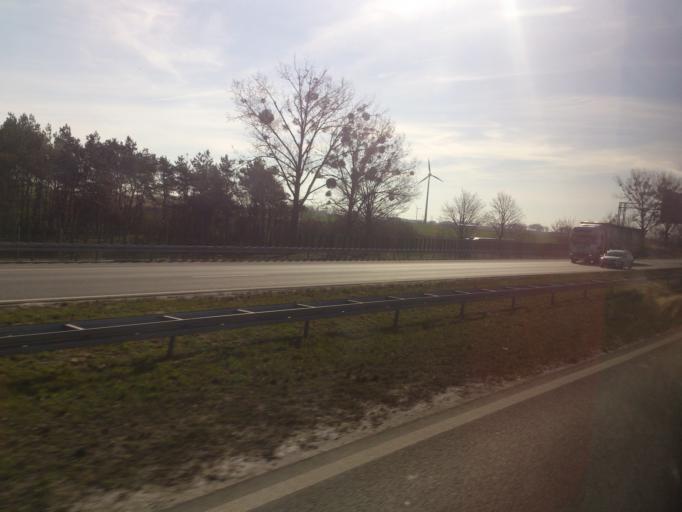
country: PL
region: Kujawsko-Pomorskie
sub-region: Powiat aleksandrowski
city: Ciechocinek
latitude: 52.8518
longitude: 18.7792
